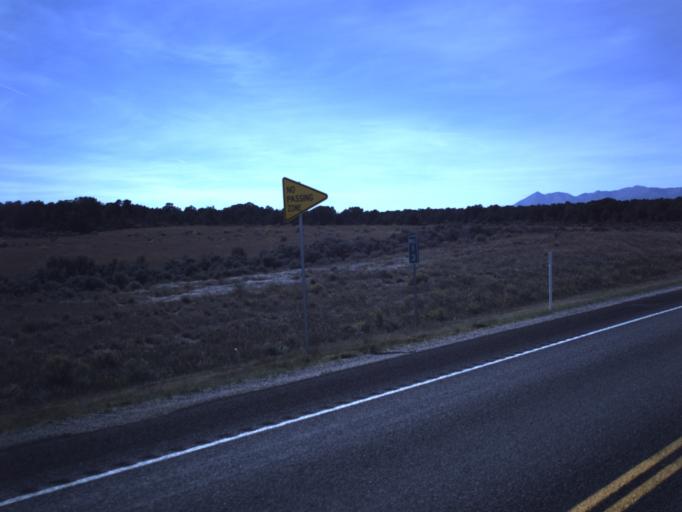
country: US
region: Colorado
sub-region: Dolores County
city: Dove Creek
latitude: 37.8363
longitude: -109.1109
